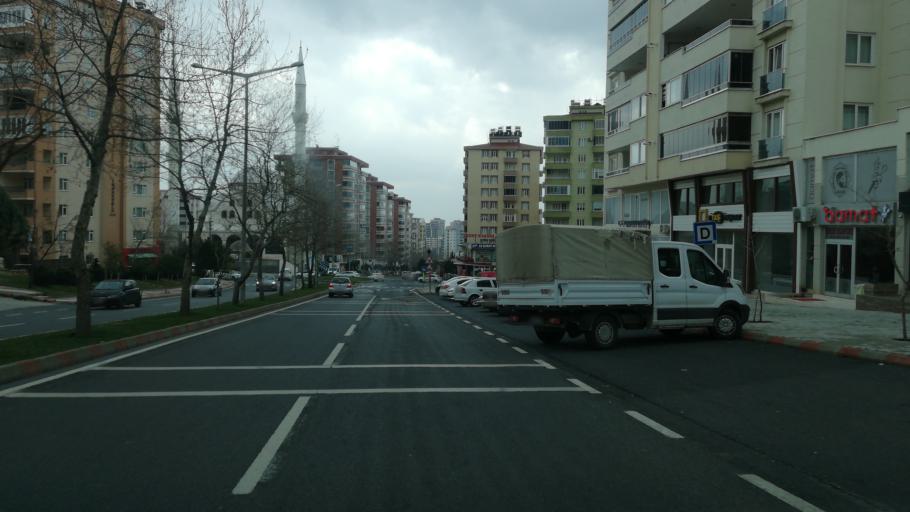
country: TR
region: Kahramanmaras
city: Kahramanmaras
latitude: 37.5878
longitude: 36.8783
